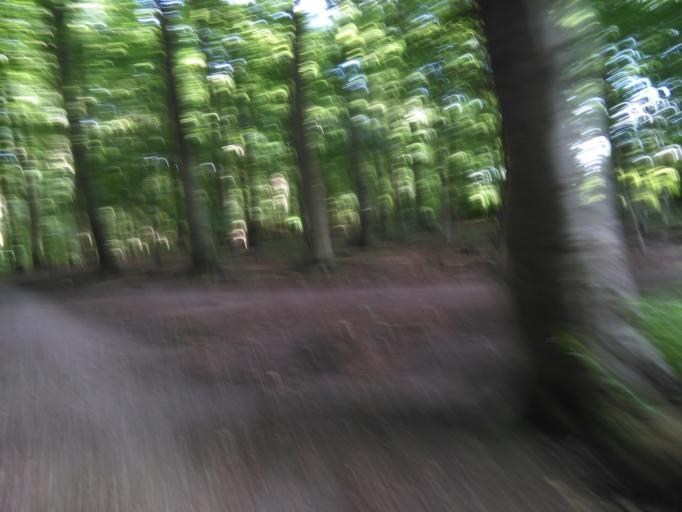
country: DK
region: Central Jutland
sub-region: Arhus Kommune
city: Arhus
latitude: 56.1167
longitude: 10.2177
